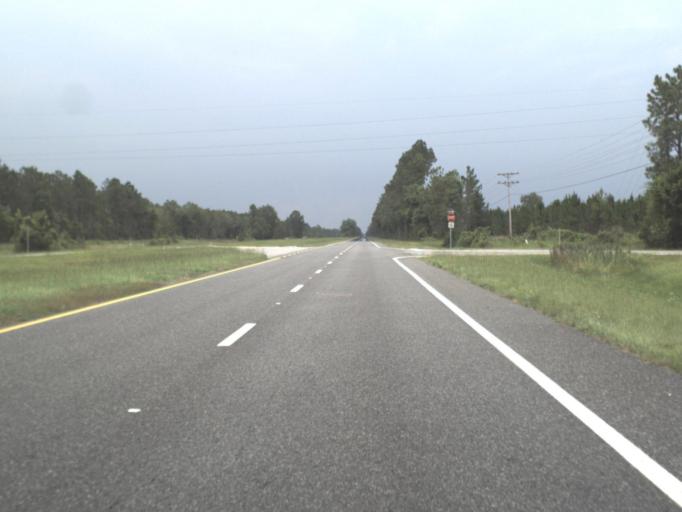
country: US
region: Florida
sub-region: Levy County
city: Bronson
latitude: 29.3168
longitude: -82.7623
